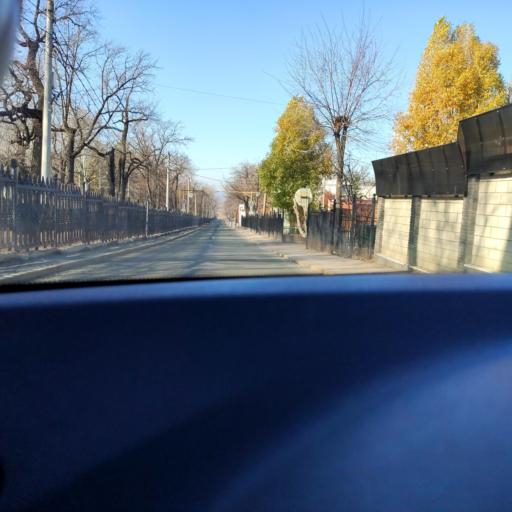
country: RU
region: Samara
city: Samara
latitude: 53.2306
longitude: 50.1691
